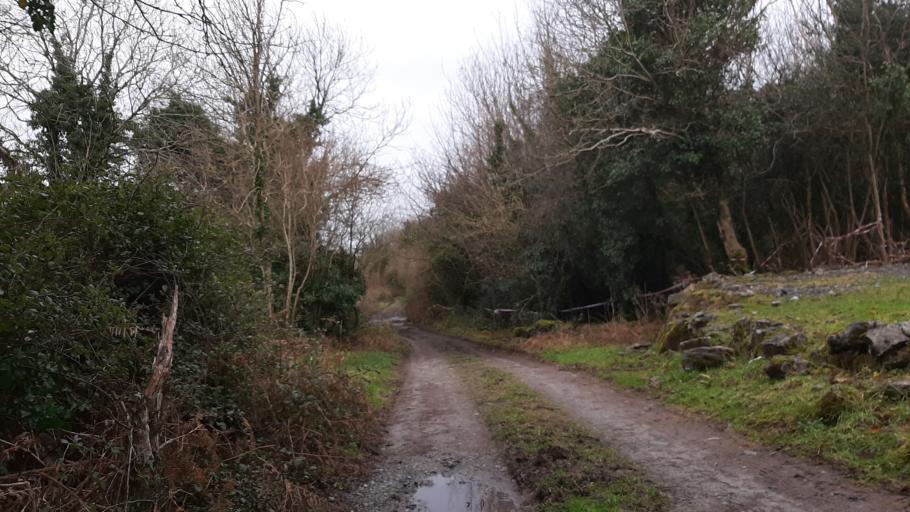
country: IE
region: Connaught
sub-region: County Galway
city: Gaillimh
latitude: 53.2962
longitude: -9.0670
